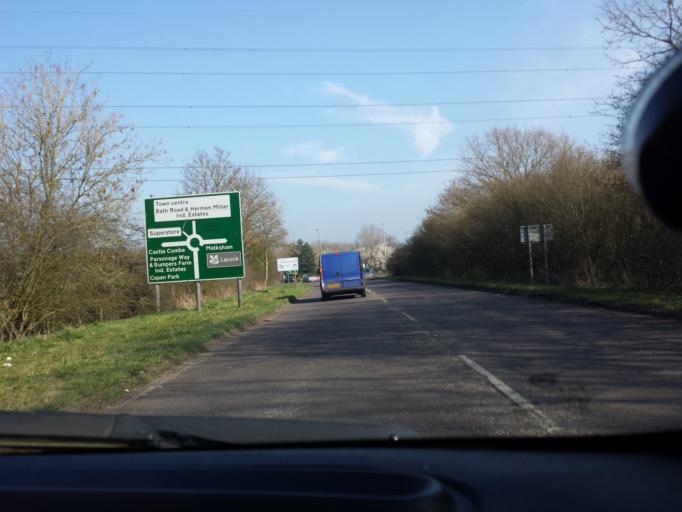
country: GB
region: England
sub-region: Wiltshire
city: Chippenham
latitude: 51.4473
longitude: -2.1520
